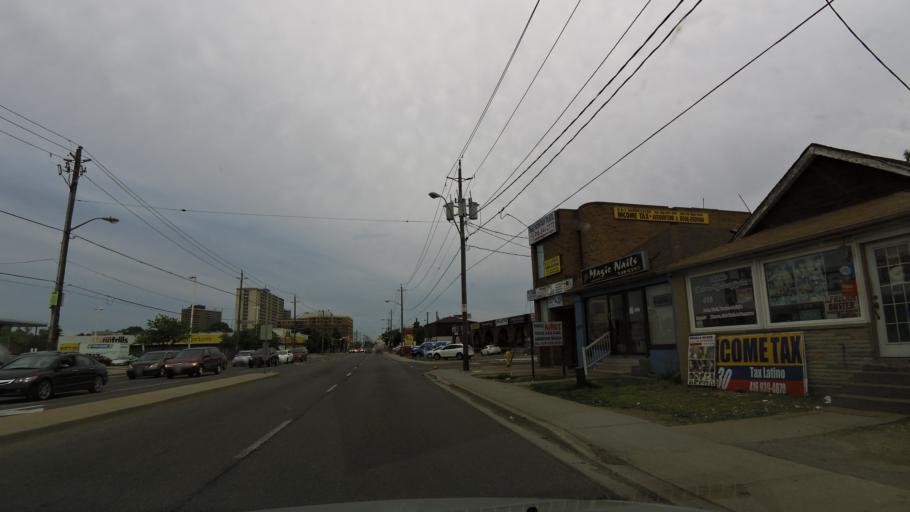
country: CA
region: Ontario
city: Etobicoke
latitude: 43.7026
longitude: -79.5038
